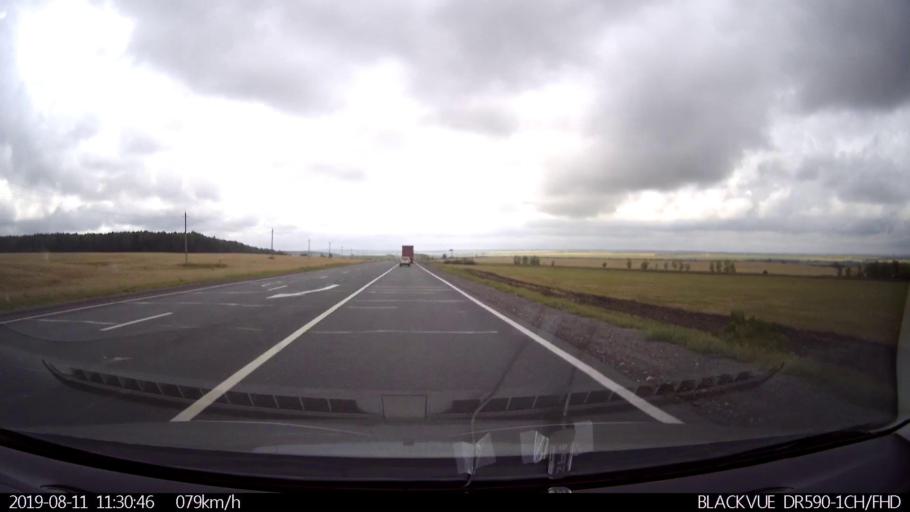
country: RU
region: Ulyanovsk
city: Krasnyy Gulyay
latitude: 54.0548
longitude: 48.2181
